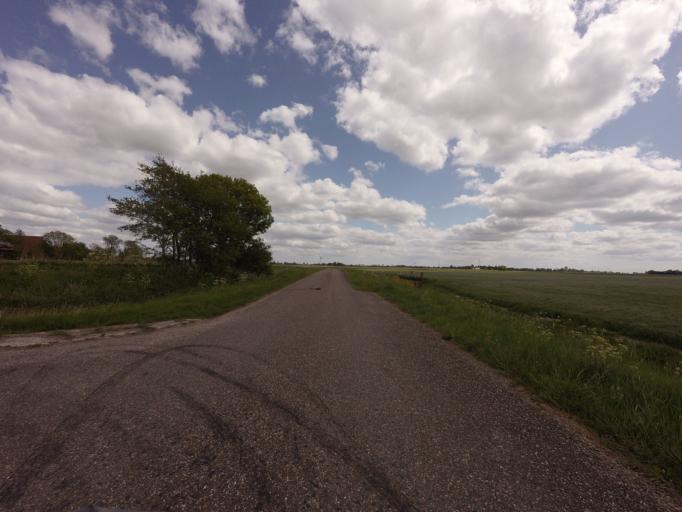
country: NL
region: Friesland
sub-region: Gemeente Franekeradeel
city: Tzum
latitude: 53.1341
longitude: 5.5633
